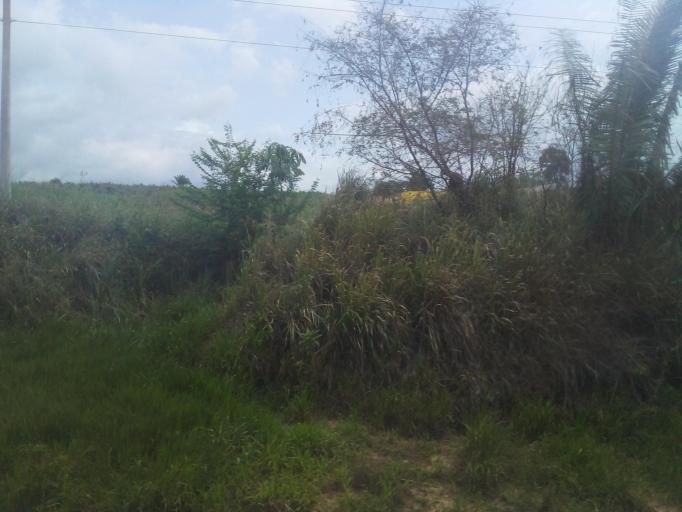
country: BR
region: Maranhao
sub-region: Santa Ines
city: Santa Ines
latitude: -3.7059
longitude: -45.9574
